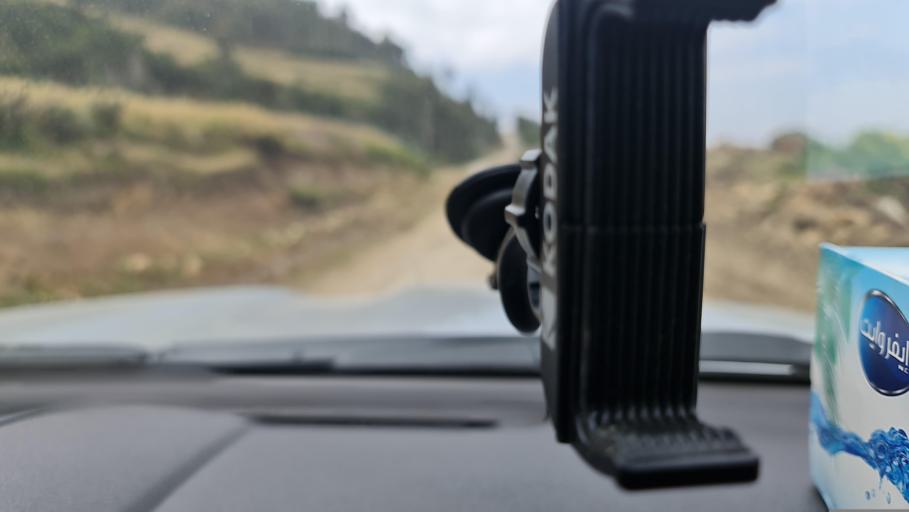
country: ET
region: Amhara
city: Abomsa
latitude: 10.1293
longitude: 39.7773
